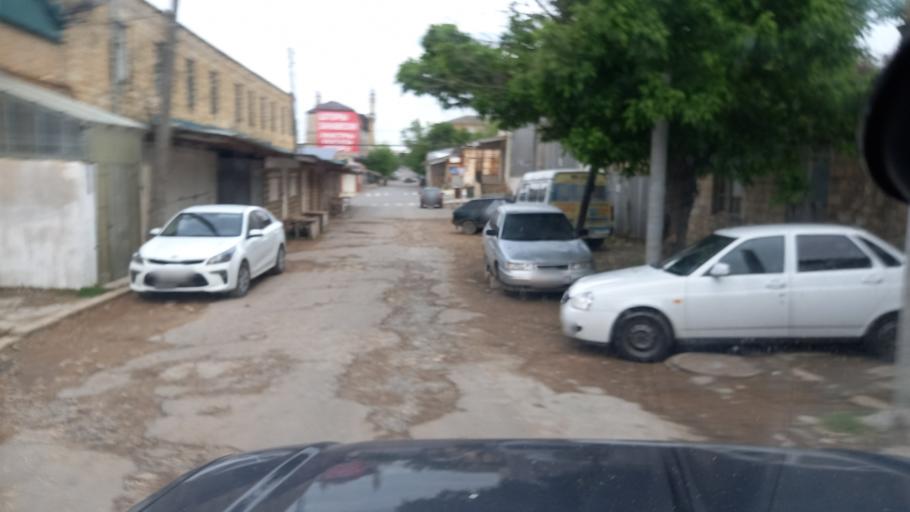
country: RU
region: Dagestan
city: Derbent
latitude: 42.0554
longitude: 48.2857
